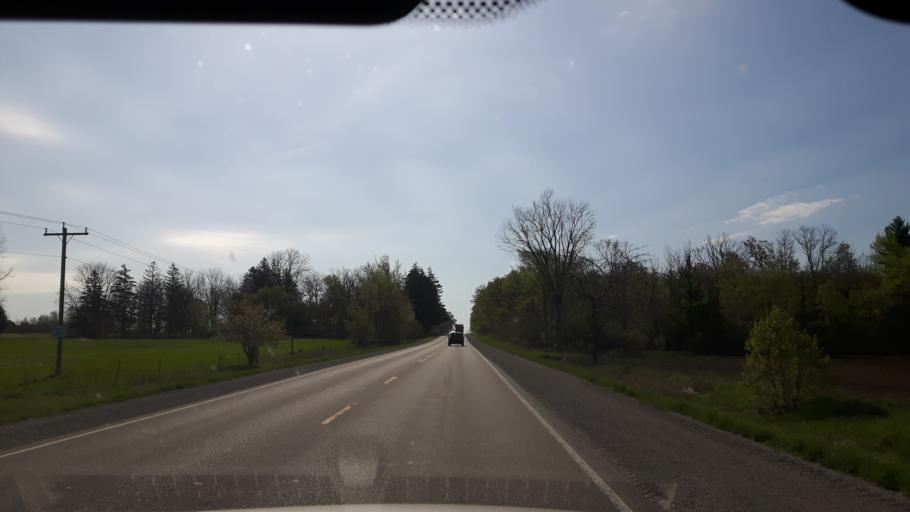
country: CA
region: Ontario
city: Bluewater
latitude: 43.5520
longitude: -81.6716
